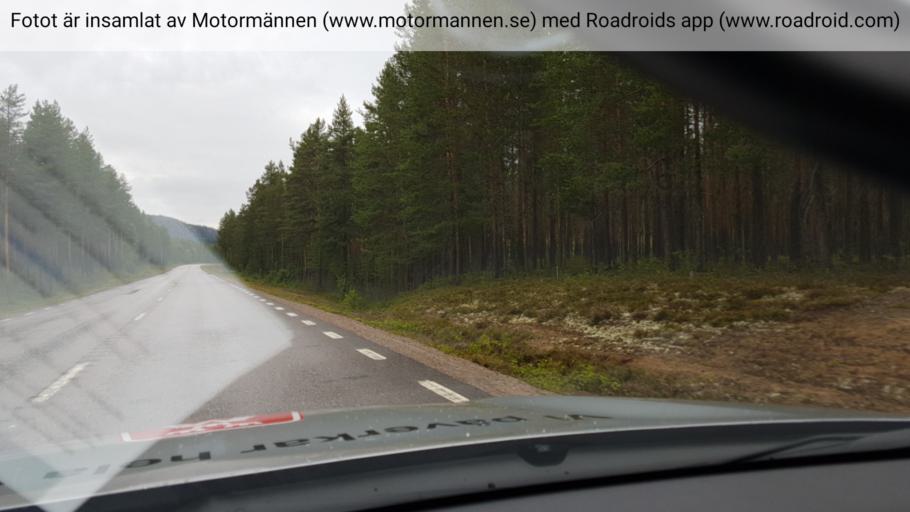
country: SE
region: Norrbotten
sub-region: Alvsbyns Kommun
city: AElvsbyn
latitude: 66.1379
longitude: 20.8913
